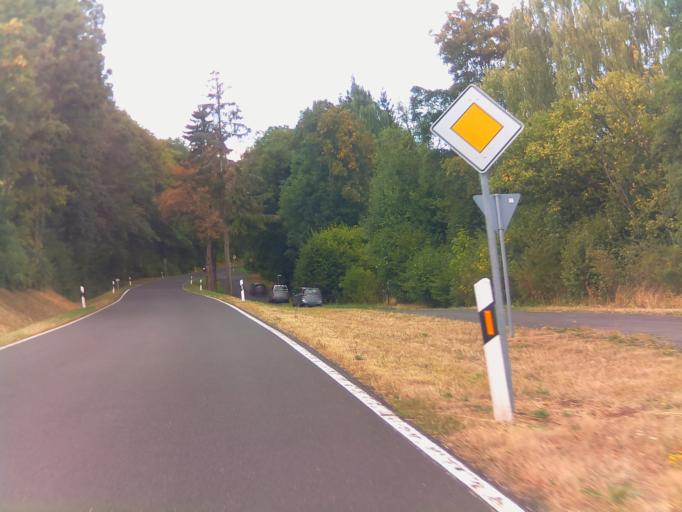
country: DE
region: Bavaria
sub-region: Regierungsbezirk Unterfranken
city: Oberelsbach
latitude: 50.4682
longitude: 10.0970
